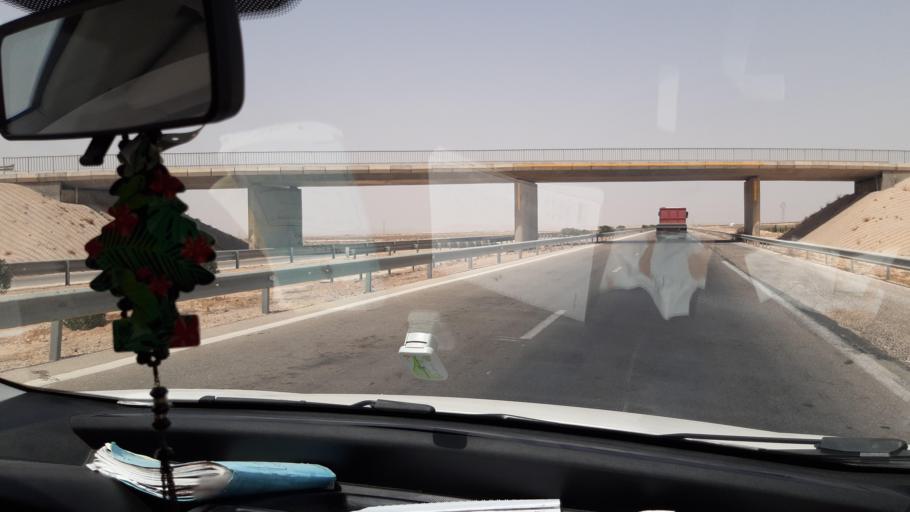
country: TN
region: Qabis
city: Gabes
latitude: 33.9330
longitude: 9.9633
